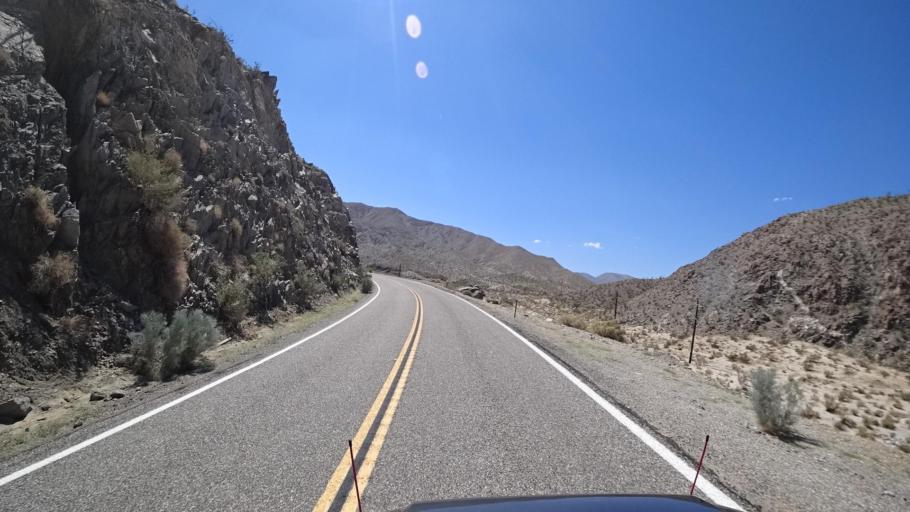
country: US
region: California
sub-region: San Diego County
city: Borrego Springs
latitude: 33.1349
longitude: -116.2997
